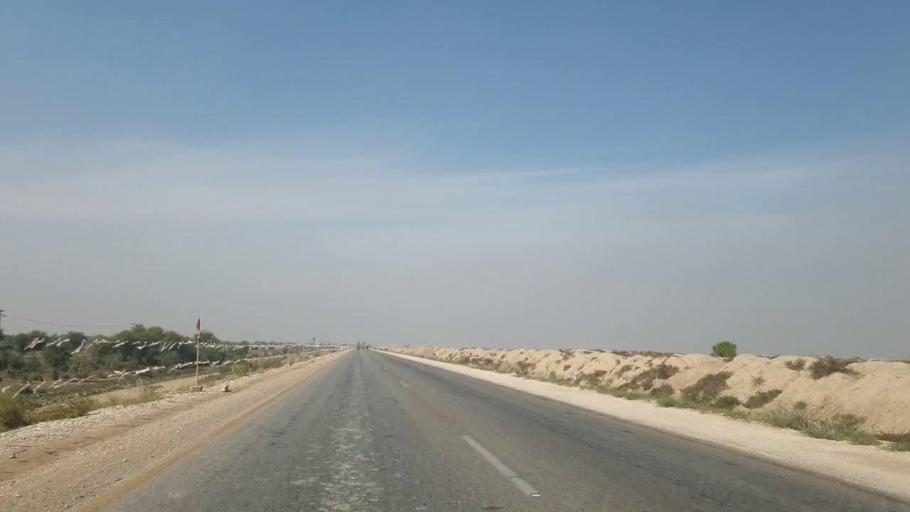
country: PK
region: Sindh
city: Sann
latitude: 25.9420
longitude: 68.2027
